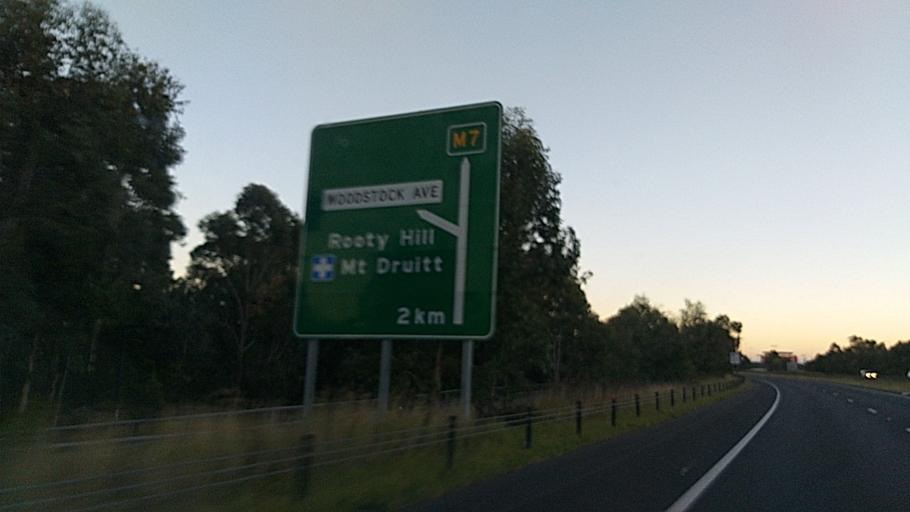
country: AU
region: New South Wales
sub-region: Blacktown
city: Doonside
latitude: -33.7814
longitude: 150.8581
